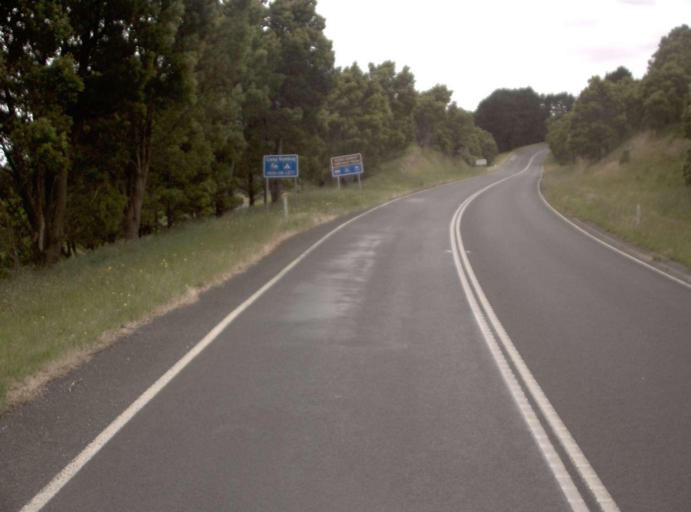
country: AU
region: Victoria
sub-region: Latrobe
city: Morwell
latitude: -38.6176
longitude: 146.1594
